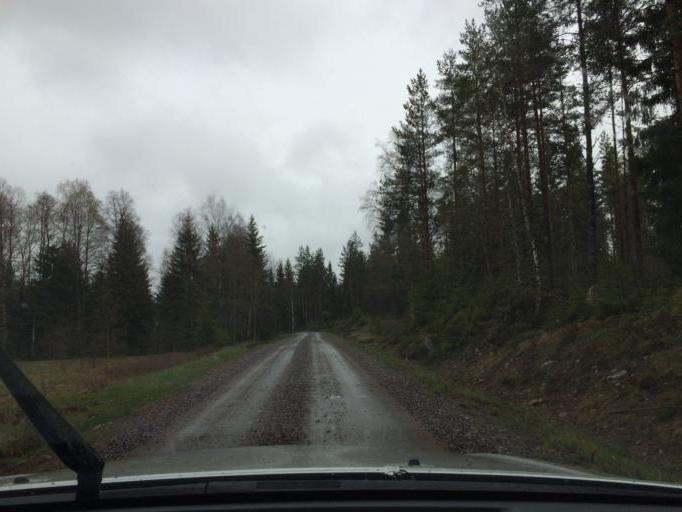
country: SE
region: OErebro
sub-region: Hallefors Kommun
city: Haellefors
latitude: 60.0388
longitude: 14.5271
